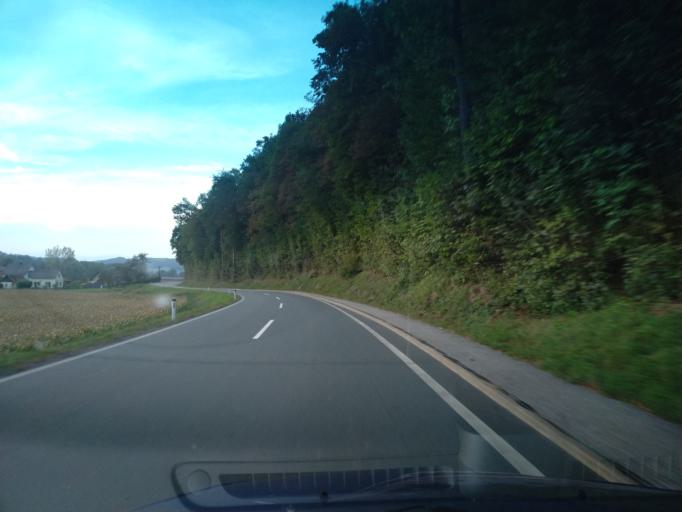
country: AT
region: Styria
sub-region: Politischer Bezirk Leibnitz
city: Arnfels
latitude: 46.6837
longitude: 15.3990
